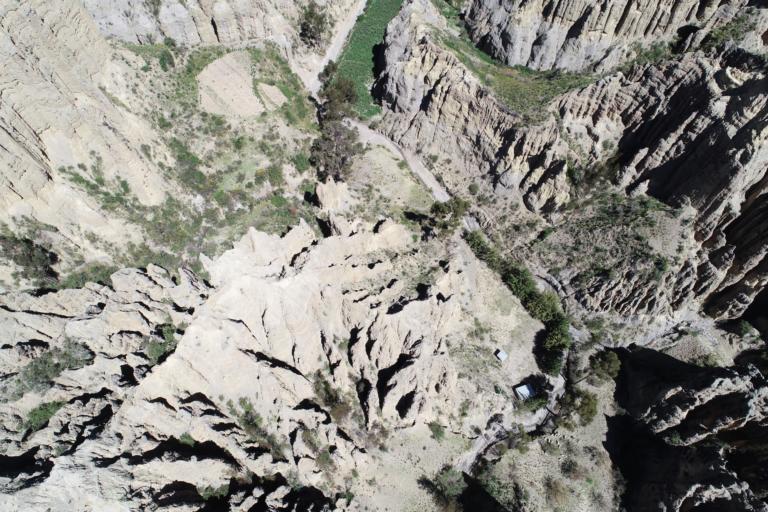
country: BO
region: La Paz
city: La Paz
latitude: -16.5048
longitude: -68.0645
